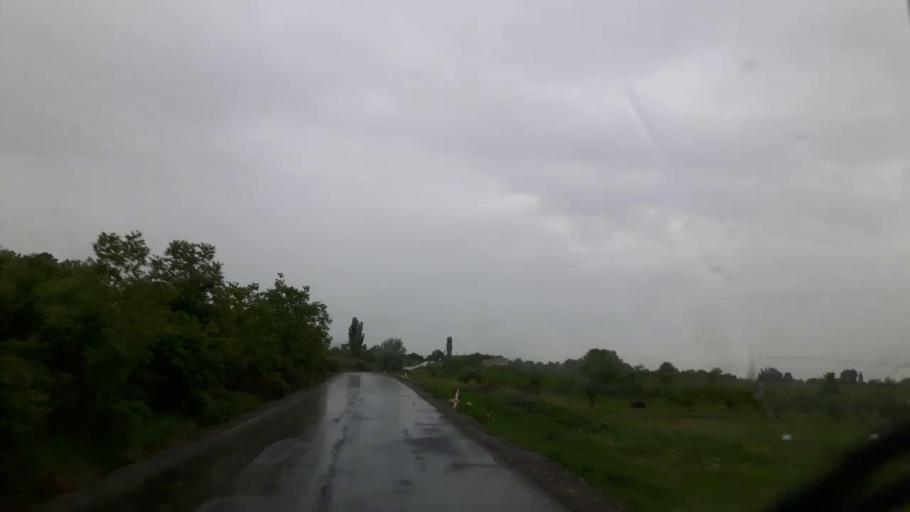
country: GE
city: Agara
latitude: 41.9833
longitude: 43.9644
